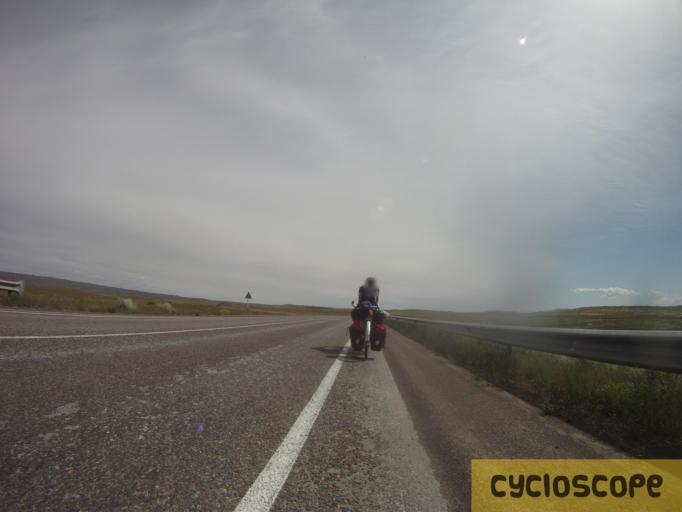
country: KZ
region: Zhambyl
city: Georgiyevka
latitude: 43.2825
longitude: 74.8554
